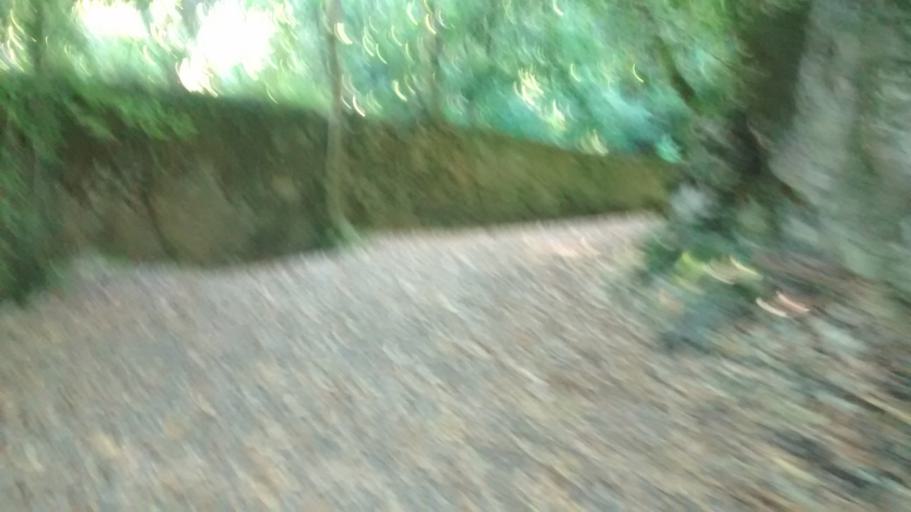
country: ES
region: Cantabria
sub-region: Provincia de Cantabria
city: Entrambasaguas
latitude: 43.3930
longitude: -3.7040
